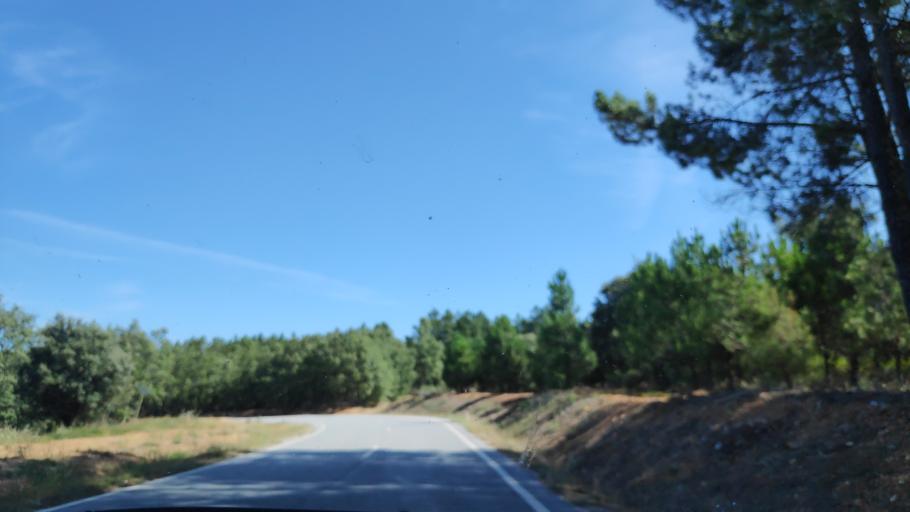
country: ES
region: Castille and Leon
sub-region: Provincia de Zamora
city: Alcanices
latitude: 41.6063
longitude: -6.3437
